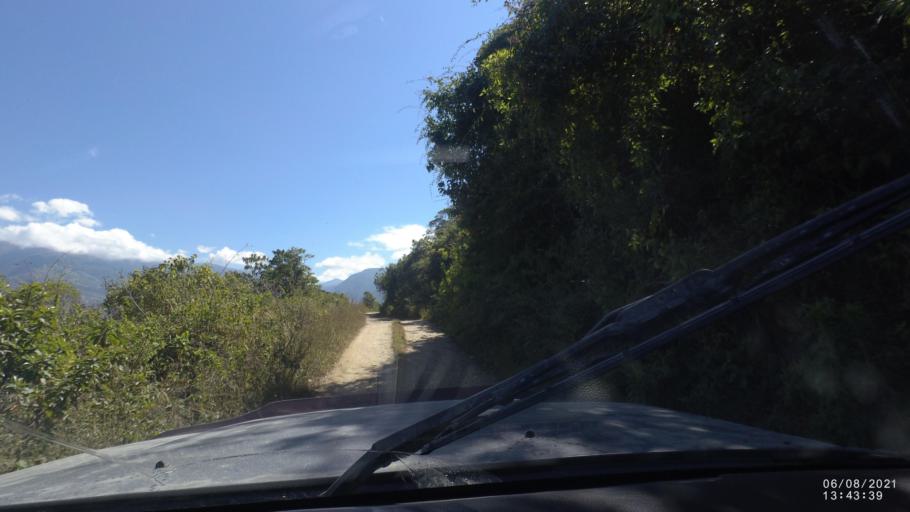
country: BO
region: La Paz
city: Quime
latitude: -16.6770
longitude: -66.7298
